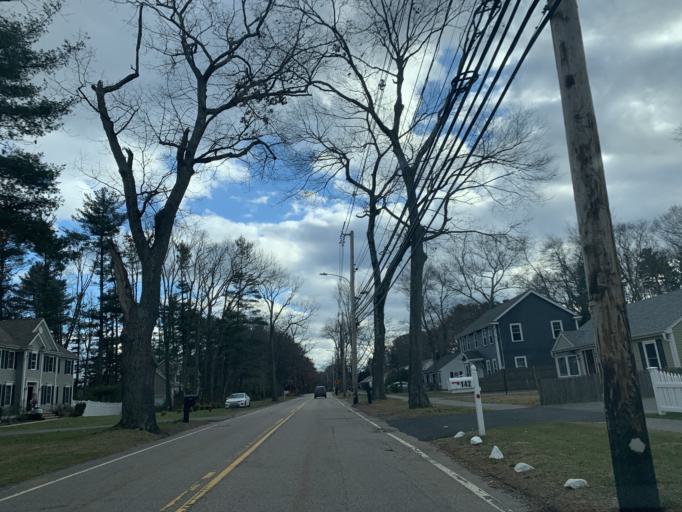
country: US
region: Massachusetts
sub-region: Norfolk County
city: Canton
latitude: 42.1800
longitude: -71.1443
